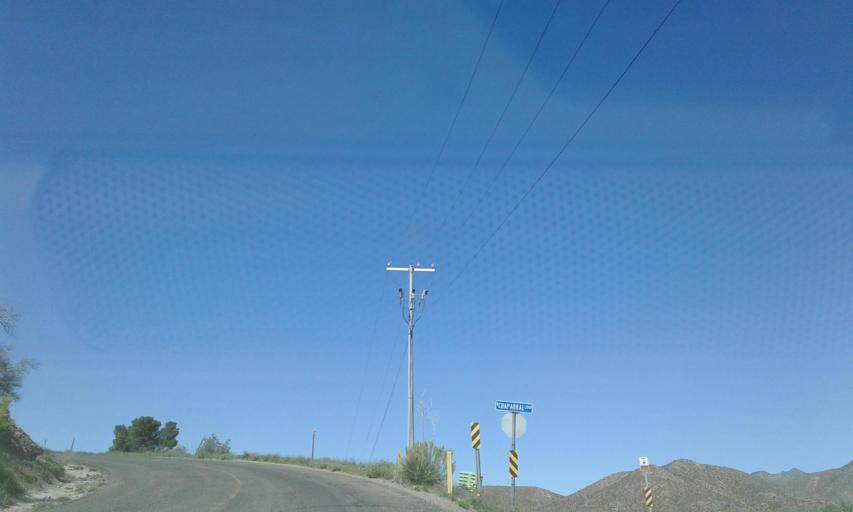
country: US
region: Arizona
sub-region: Gila County
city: Central Heights-Midland City
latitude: 33.4224
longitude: -110.8126
